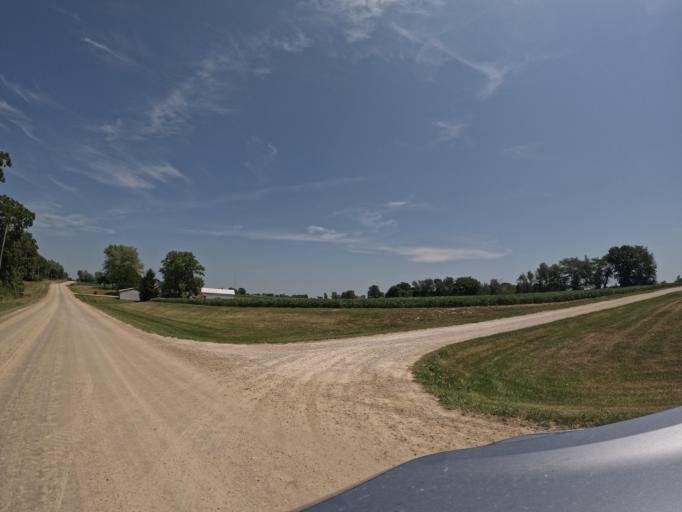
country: US
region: Iowa
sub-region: Henry County
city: Mount Pleasant
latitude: 40.9462
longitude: -91.6079
